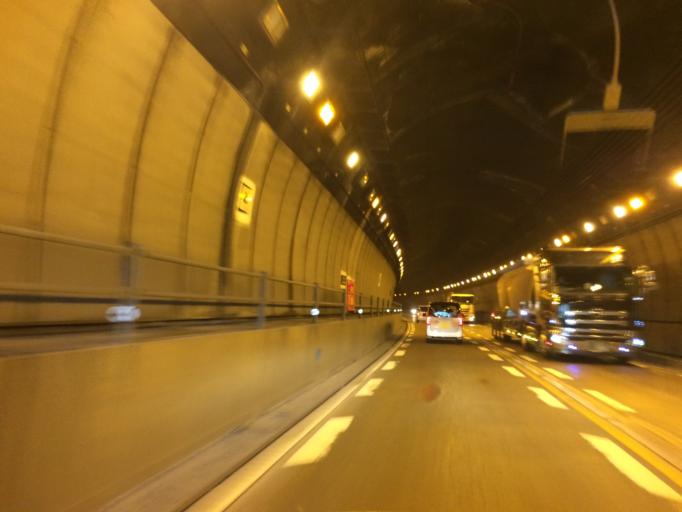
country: JP
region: Shizuoka
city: Shimada
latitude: 34.8556
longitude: 138.2060
